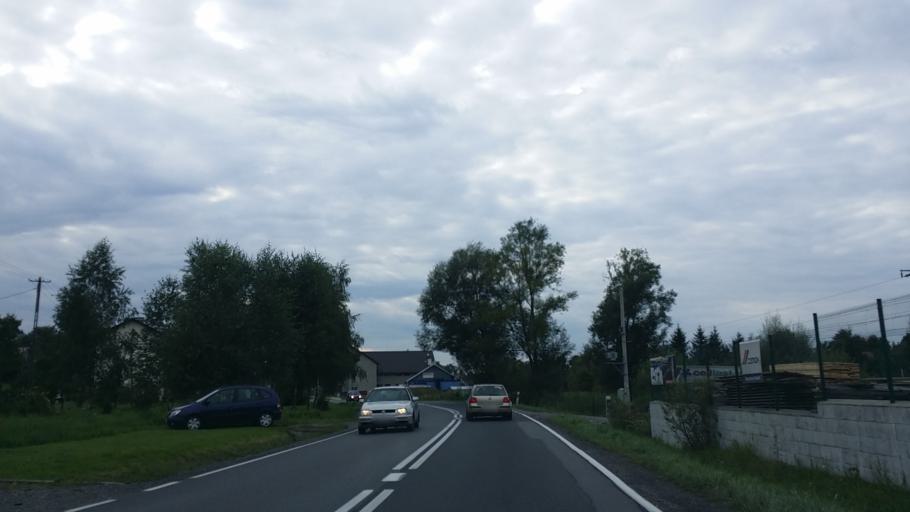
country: PL
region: Lesser Poland Voivodeship
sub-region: Powiat wadowicki
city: Brzeznica
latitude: 49.9641
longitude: 19.6442
